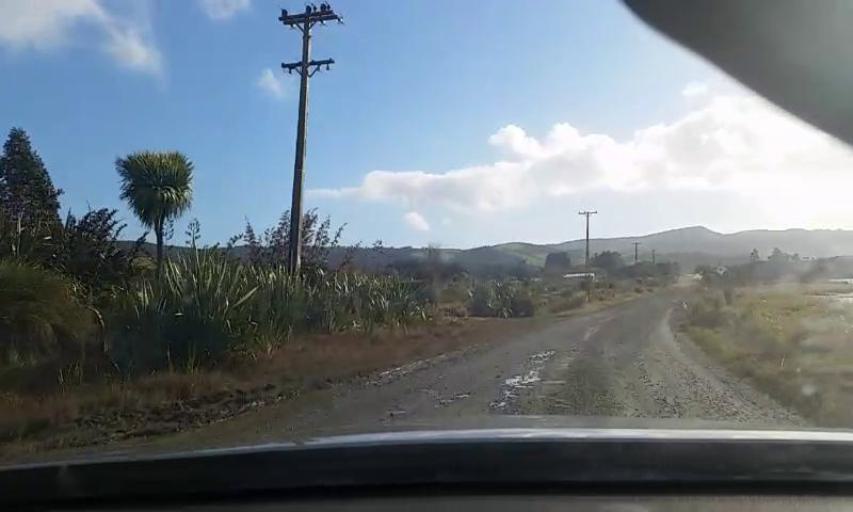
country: NZ
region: Otago
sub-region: Clutha District
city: Papatowai
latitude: -46.6280
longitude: 169.1366
